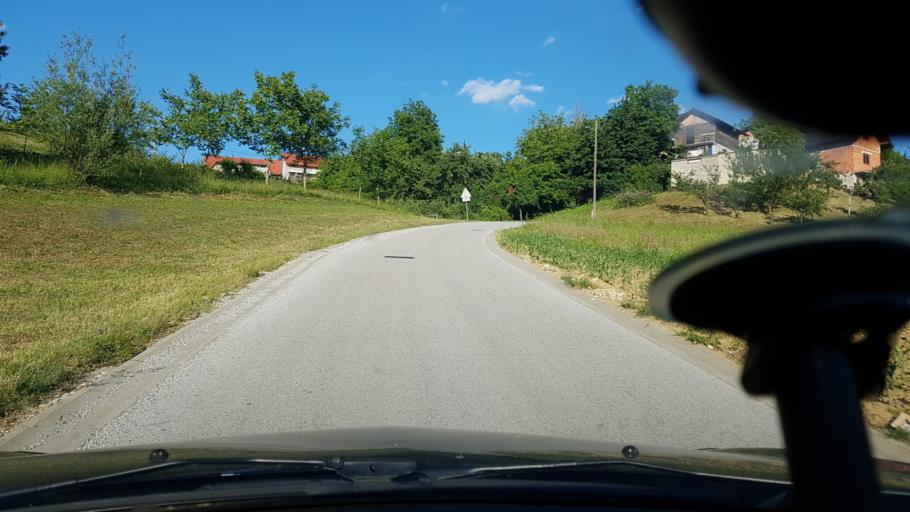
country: HR
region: Krapinsko-Zagorska
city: Radoboj
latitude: 46.2091
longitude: 15.9055
